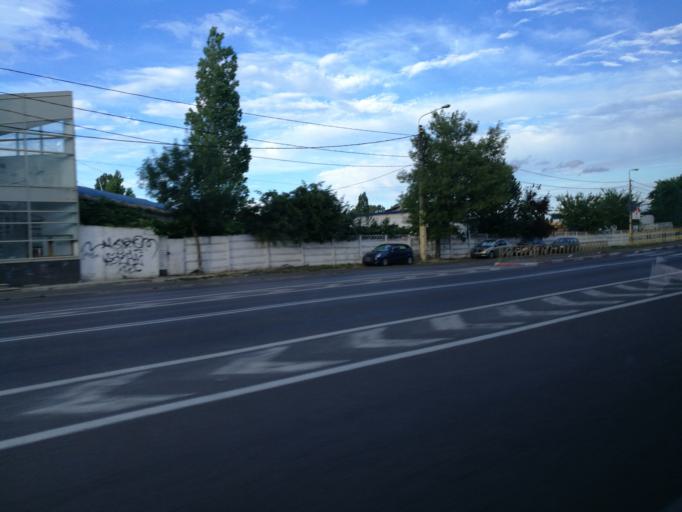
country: RO
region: Constanta
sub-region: Municipiul Constanta
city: Constanta
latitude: 44.1516
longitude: 28.6228
